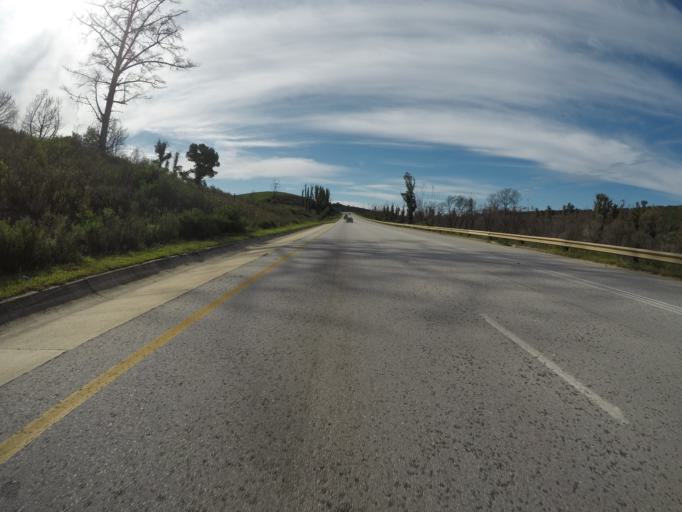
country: ZA
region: Eastern Cape
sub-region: Cacadu District Municipality
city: Jeffrey's Bay
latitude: -33.9032
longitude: 25.1038
